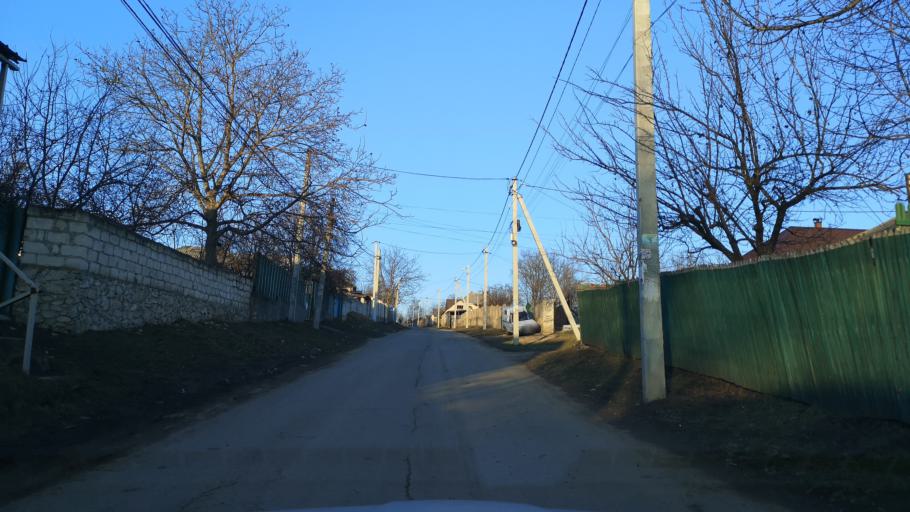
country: MD
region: Orhei
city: Orhei
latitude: 47.3569
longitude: 28.6896
